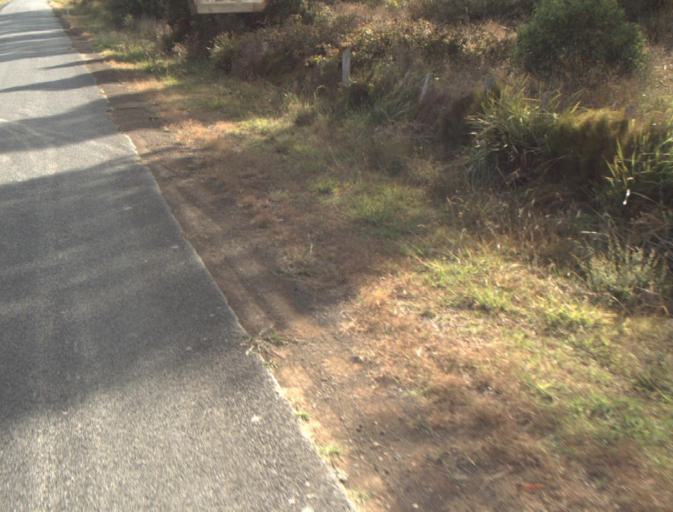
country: AU
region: Tasmania
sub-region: Launceston
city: Mayfield
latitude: -41.2389
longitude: 147.1776
